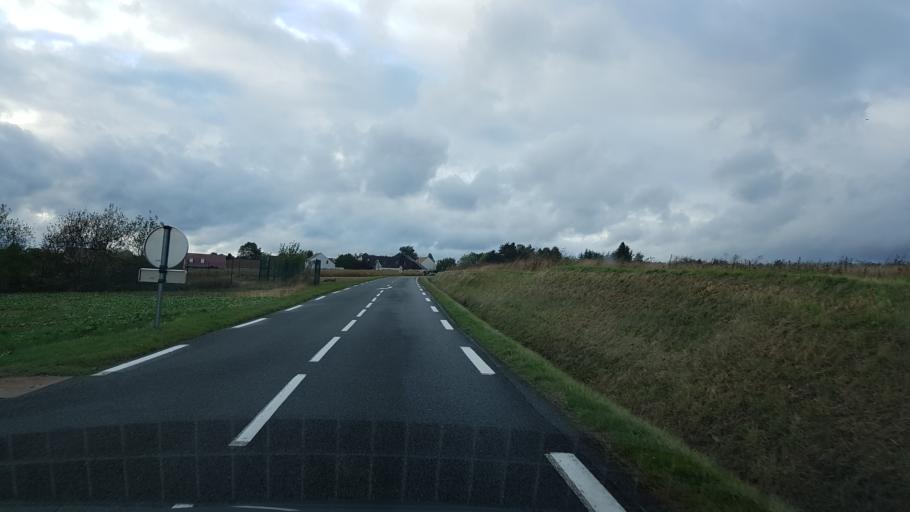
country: FR
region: Ile-de-France
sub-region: Departement de l'Essonne
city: Gometz-la-Ville
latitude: 48.6673
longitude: 2.1327
